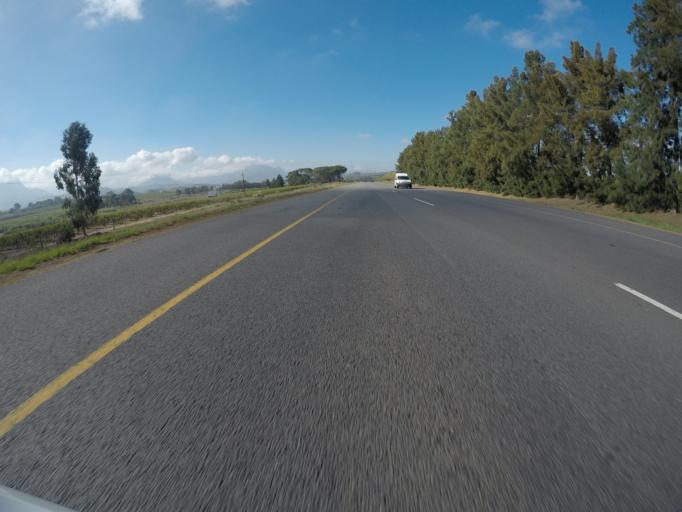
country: ZA
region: Western Cape
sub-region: Cape Winelands District Municipality
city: Stellenbosch
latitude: -33.8661
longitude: 18.8124
